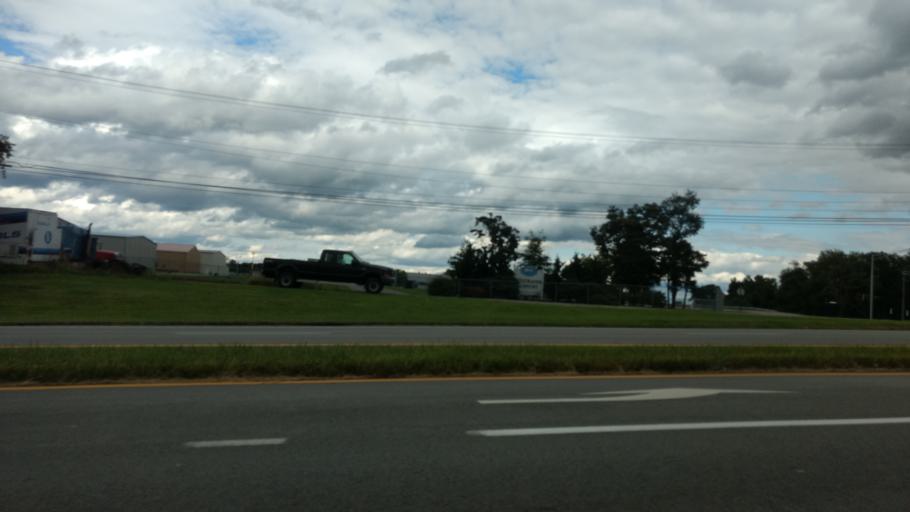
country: US
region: Pennsylvania
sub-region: Westmoreland County
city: Fellsburg
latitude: 40.2046
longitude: -79.8383
